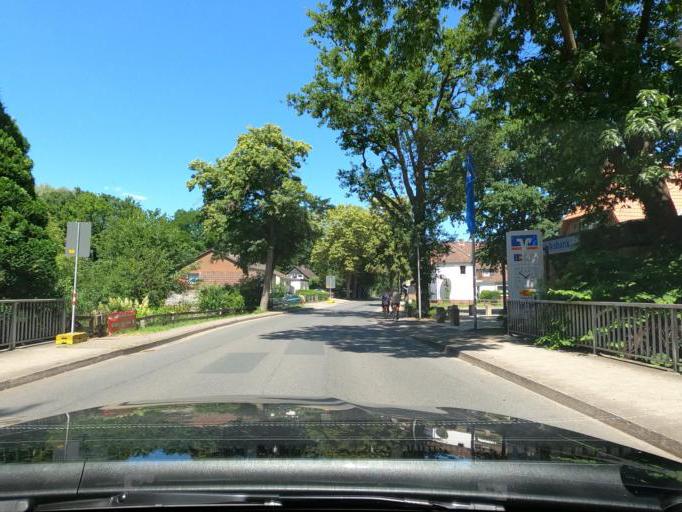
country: DE
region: Lower Saxony
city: Wienhausen
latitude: 52.5805
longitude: 10.1894
